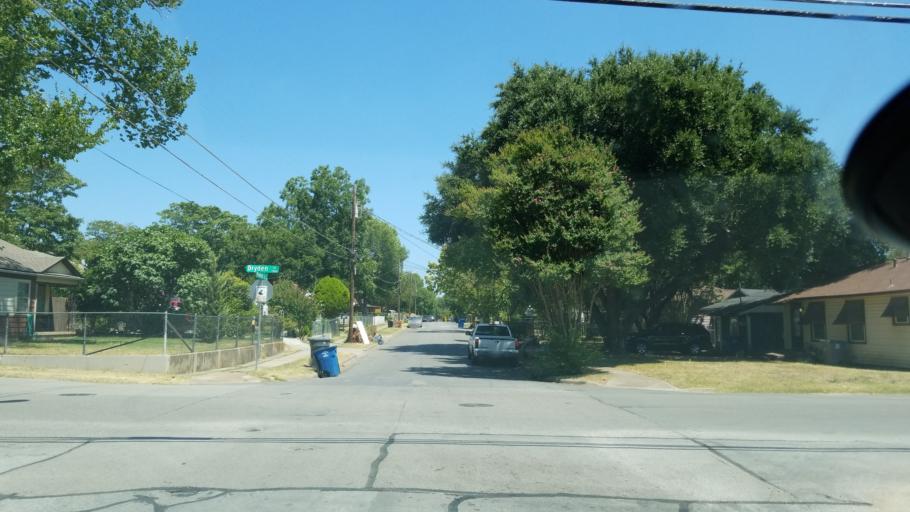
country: US
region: Texas
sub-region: Dallas County
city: Cockrell Hill
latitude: 32.7244
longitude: -96.8853
